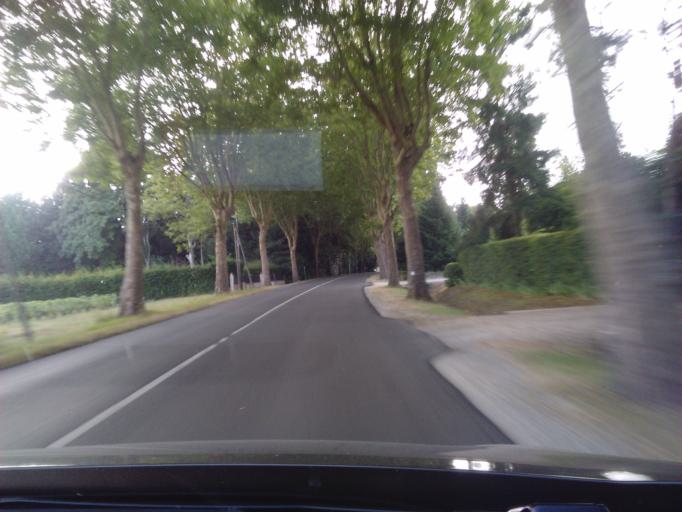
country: FR
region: Centre
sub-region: Departement du Loir-et-Cher
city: Cellettes
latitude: 47.5198
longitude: 1.3942
